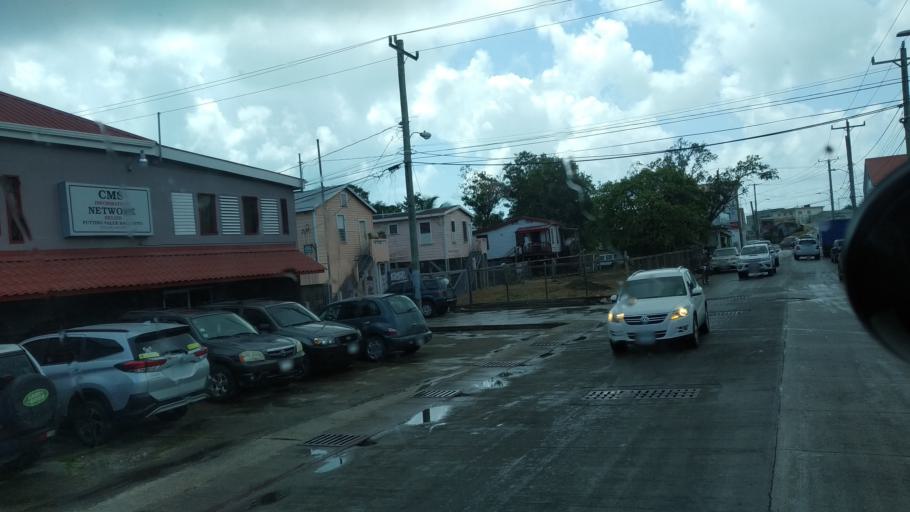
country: BZ
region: Belize
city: Belize City
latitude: 17.5006
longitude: -88.1910
